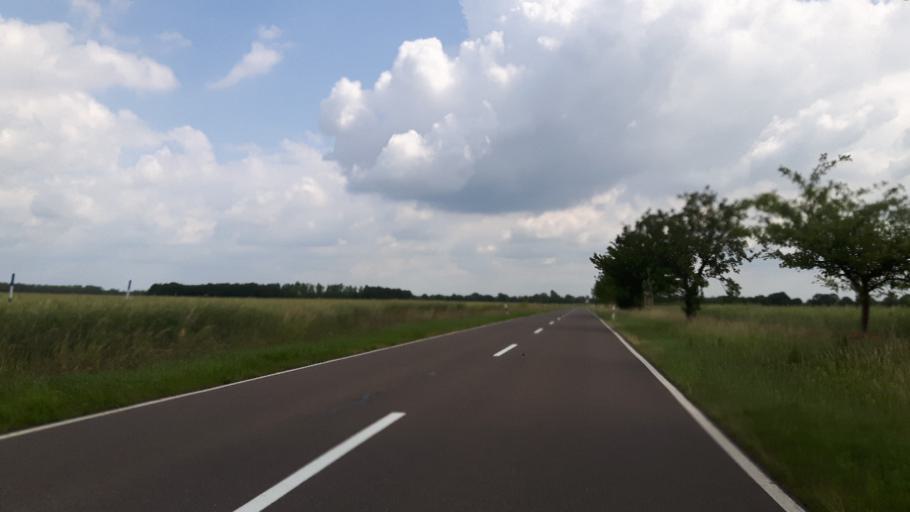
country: DE
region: Saxony
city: Delitzsch
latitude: 51.5477
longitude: 12.3745
